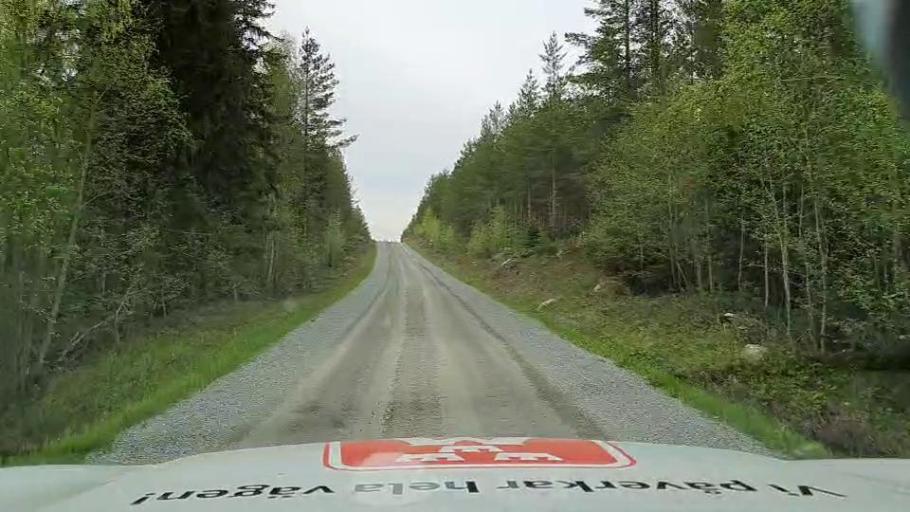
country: SE
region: Jaemtland
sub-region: Braecke Kommun
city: Braecke
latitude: 62.4662
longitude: 14.9185
